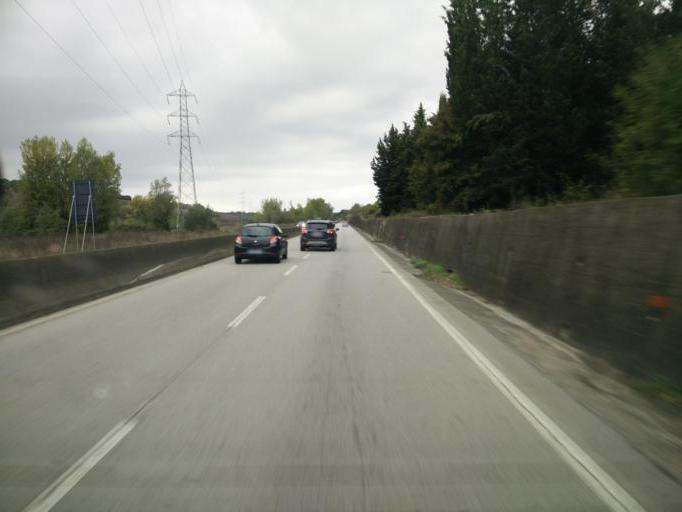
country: IT
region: Tuscany
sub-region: Provincia di Siena
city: Siena
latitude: 43.3213
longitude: 11.2997
